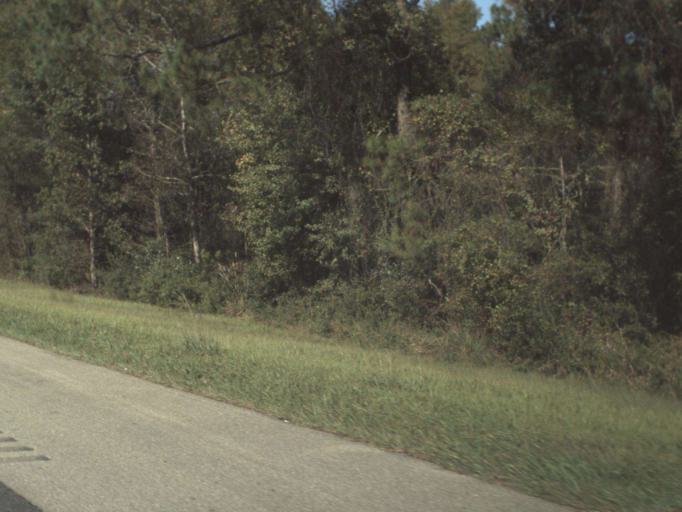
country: US
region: Florida
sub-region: Washington County
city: Chipley
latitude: 30.7463
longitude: -85.4390
